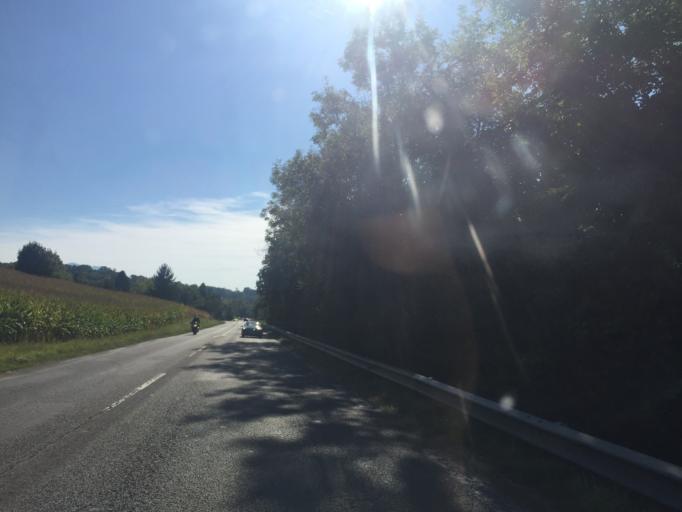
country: FR
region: Rhone-Alpes
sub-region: Departement de la Haute-Savoie
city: Viuz-la-Chiesaz
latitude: 45.8346
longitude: 6.0556
